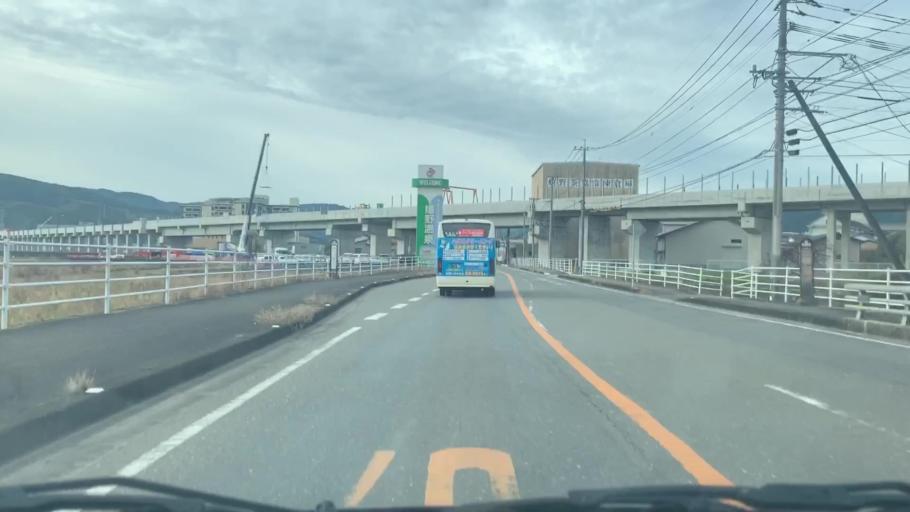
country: JP
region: Saga Prefecture
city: Ureshinomachi-shimojuku
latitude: 33.1098
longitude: 130.0000
